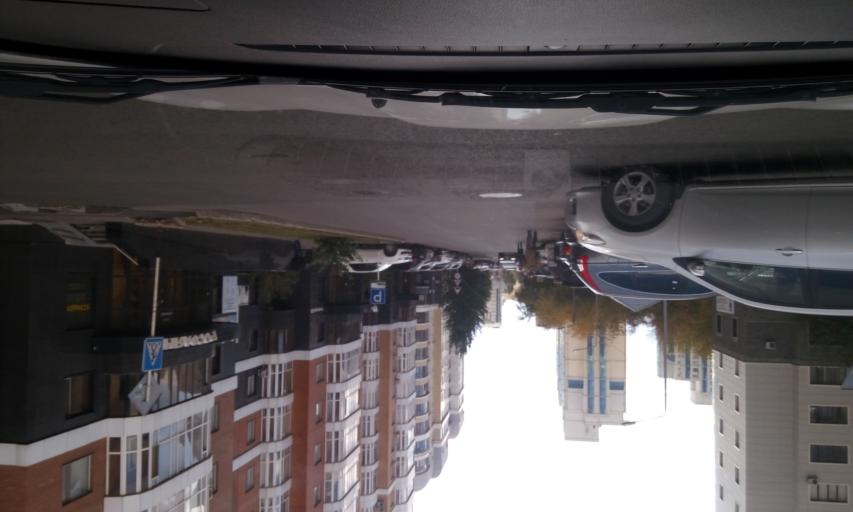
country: KZ
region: Astana Qalasy
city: Astana
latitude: 51.1681
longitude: 71.4310
